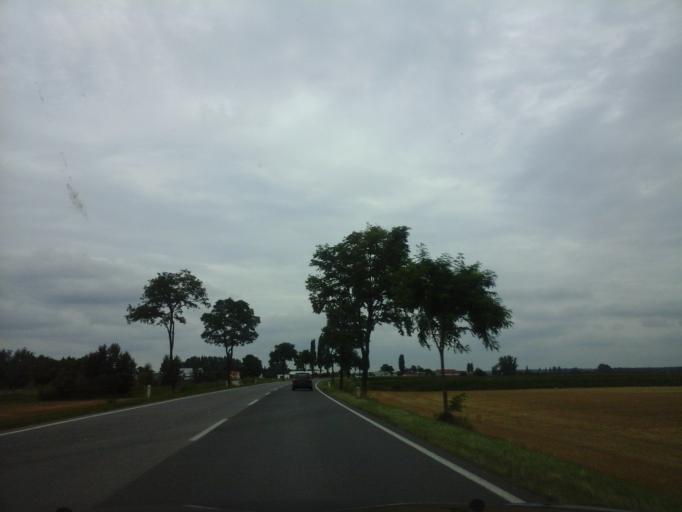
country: AT
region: Lower Austria
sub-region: Politischer Bezirk Ganserndorf
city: Engelhartstetten
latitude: 48.1723
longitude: 16.8919
